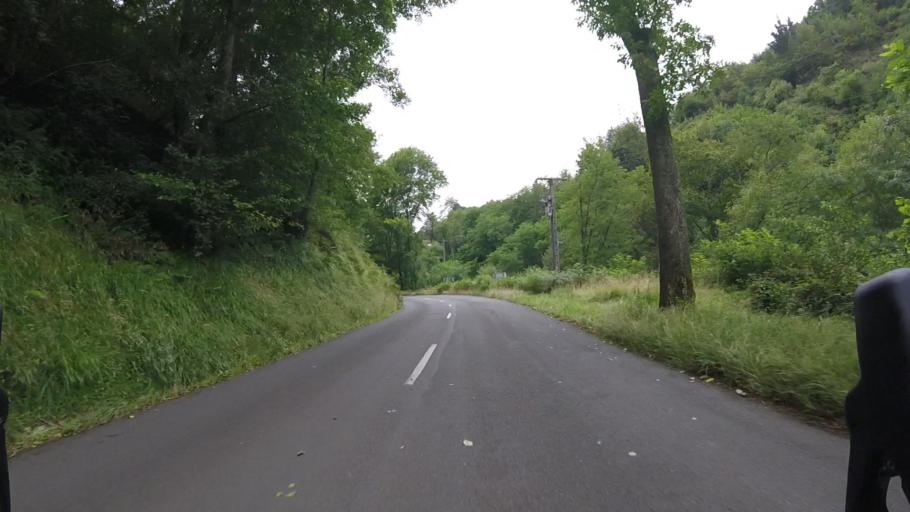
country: ES
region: Basque Country
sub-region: Provincia de Guipuzcoa
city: Irun
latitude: 43.2854
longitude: -1.8249
